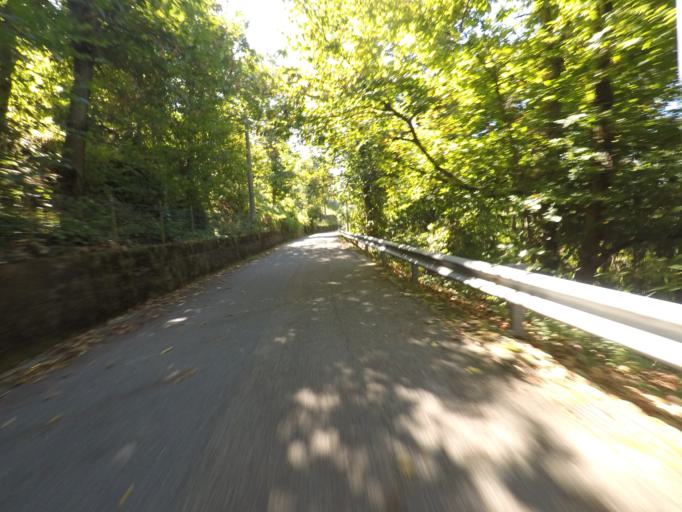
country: IT
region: Tuscany
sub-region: Provincia di Massa-Carrara
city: Montignoso
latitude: 44.0331
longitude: 10.1640
